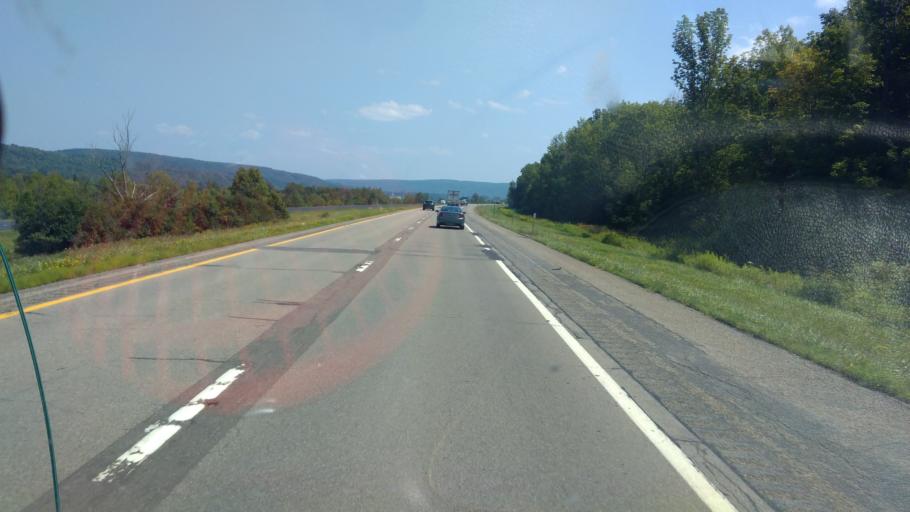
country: US
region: New York
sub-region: Allegany County
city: Alfred
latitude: 42.3175
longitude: -77.8076
